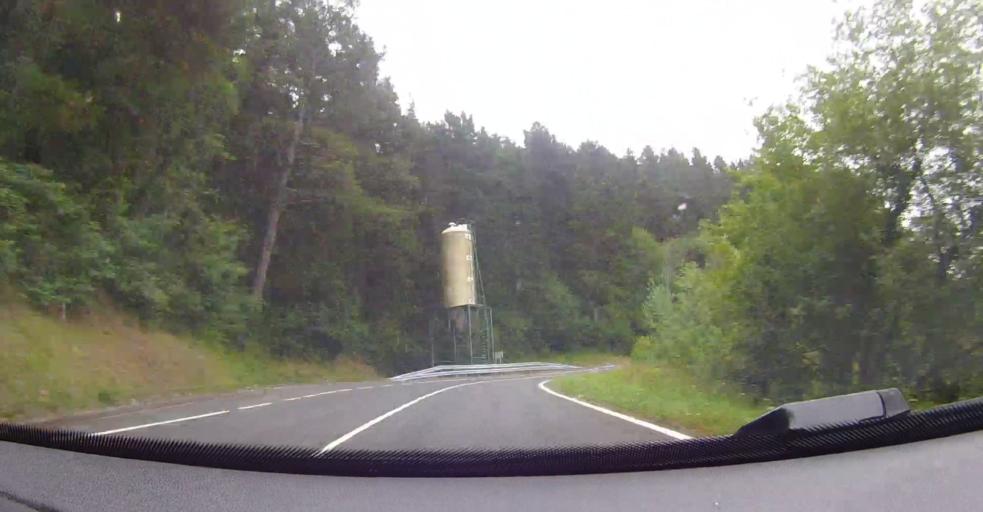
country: ES
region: Basque Country
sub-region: Bizkaia
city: Balmaseda
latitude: 43.2440
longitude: -3.3003
